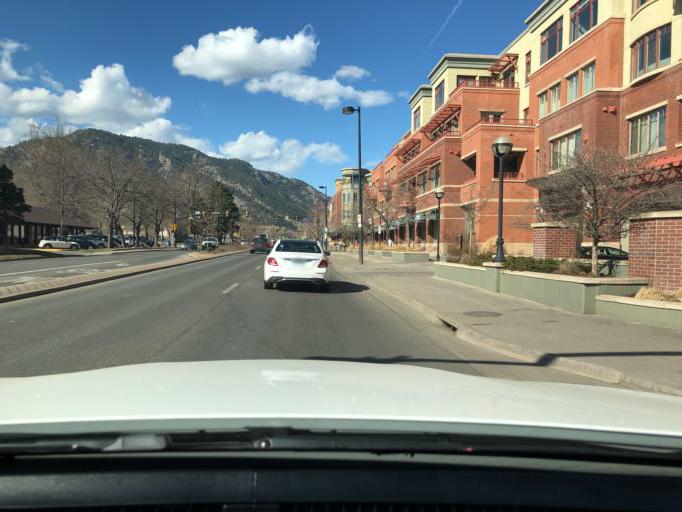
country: US
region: Colorado
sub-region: Boulder County
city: Boulder
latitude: 40.0165
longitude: -105.2767
